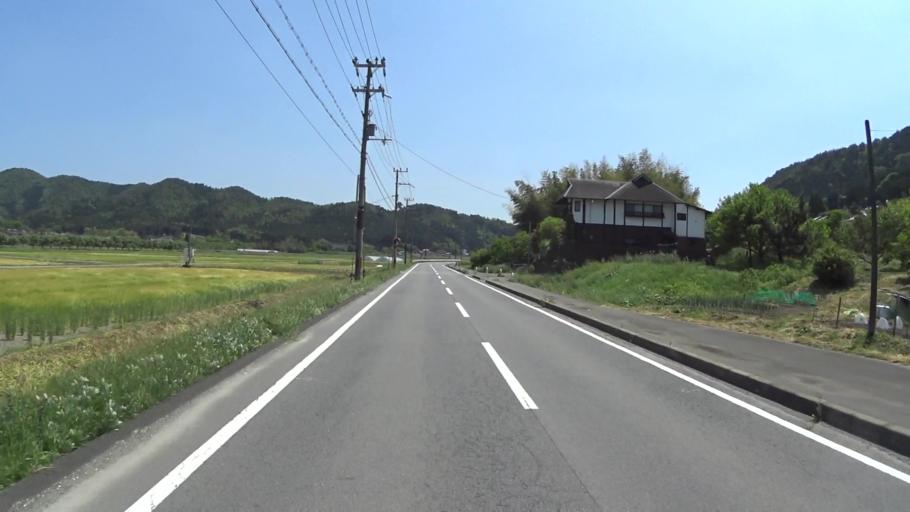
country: JP
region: Kyoto
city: Kameoka
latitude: 35.0232
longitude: 135.4877
